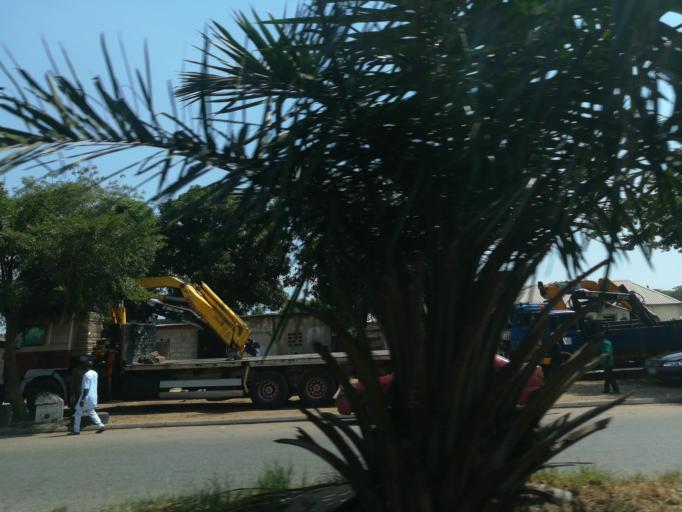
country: NG
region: Abuja Federal Capital Territory
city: Abuja
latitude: 9.0707
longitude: 7.4461
